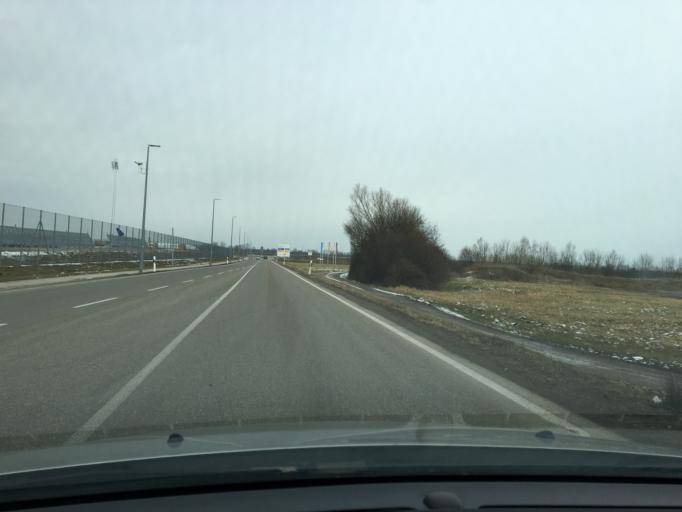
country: DE
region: Bavaria
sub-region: Upper Bavaria
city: Marzling
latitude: 48.3581
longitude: 11.8061
